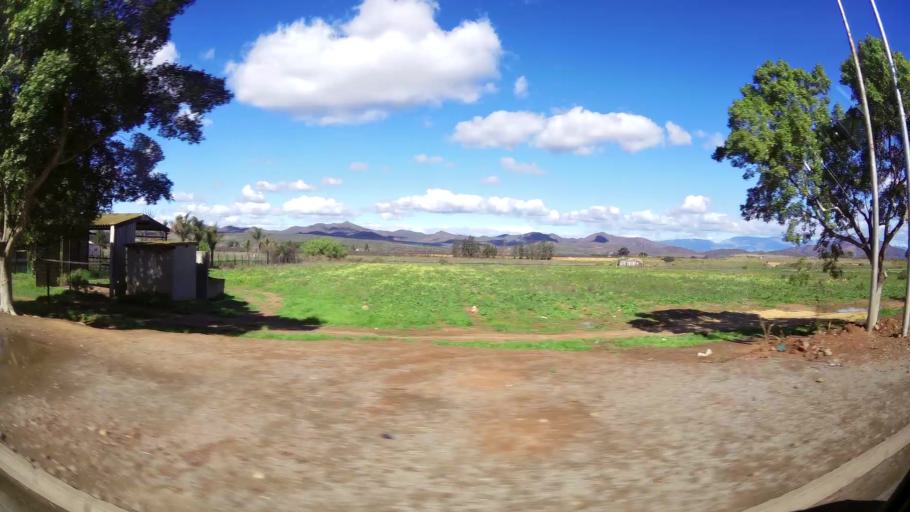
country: ZA
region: Western Cape
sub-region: Cape Winelands District Municipality
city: Ashton
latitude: -33.8354
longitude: 20.0487
